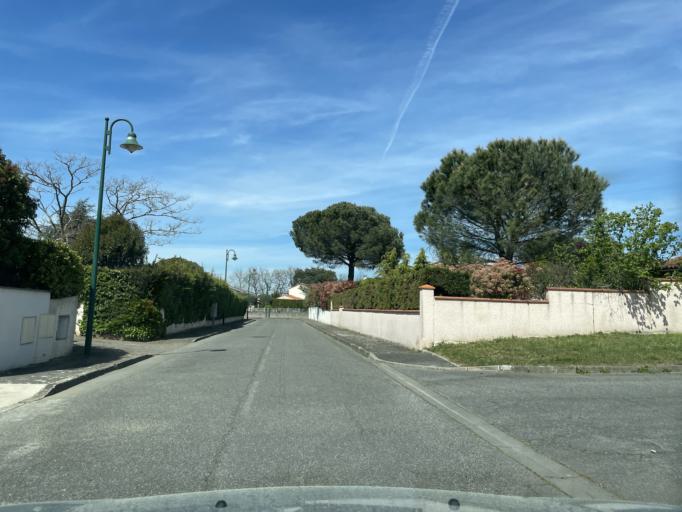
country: FR
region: Midi-Pyrenees
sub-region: Departement de la Haute-Garonne
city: Pibrac
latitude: 43.6161
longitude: 1.2692
